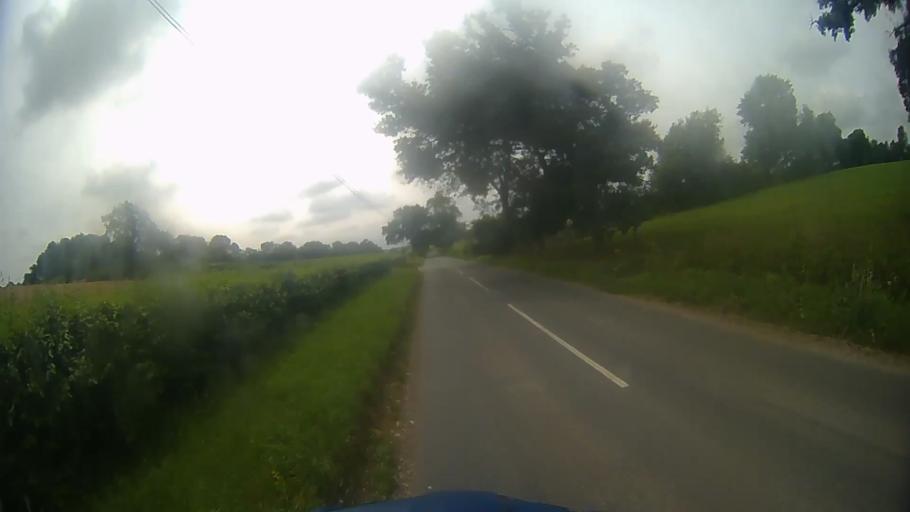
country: GB
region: England
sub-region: Hampshire
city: Overton
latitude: 51.2646
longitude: -1.3128
